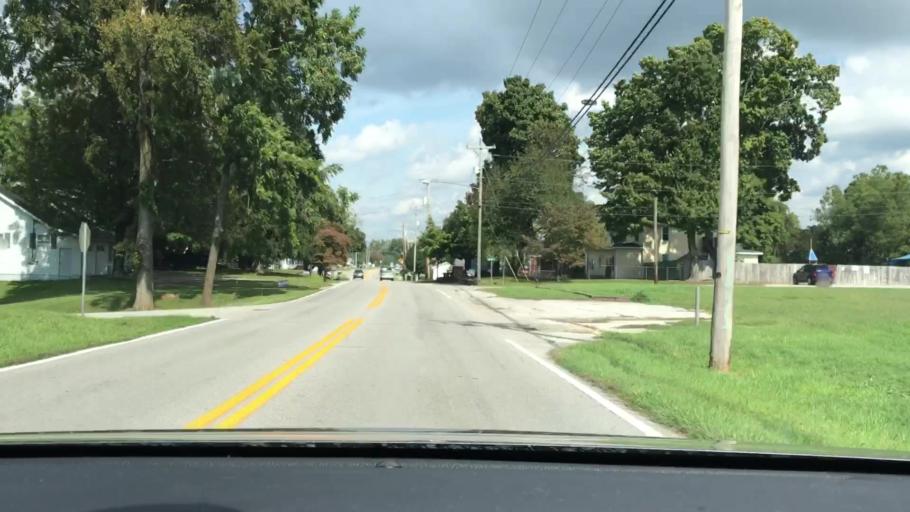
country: US
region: Kentucky
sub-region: Pulaski County
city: Somerset
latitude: 37.0728
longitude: -84.6160
